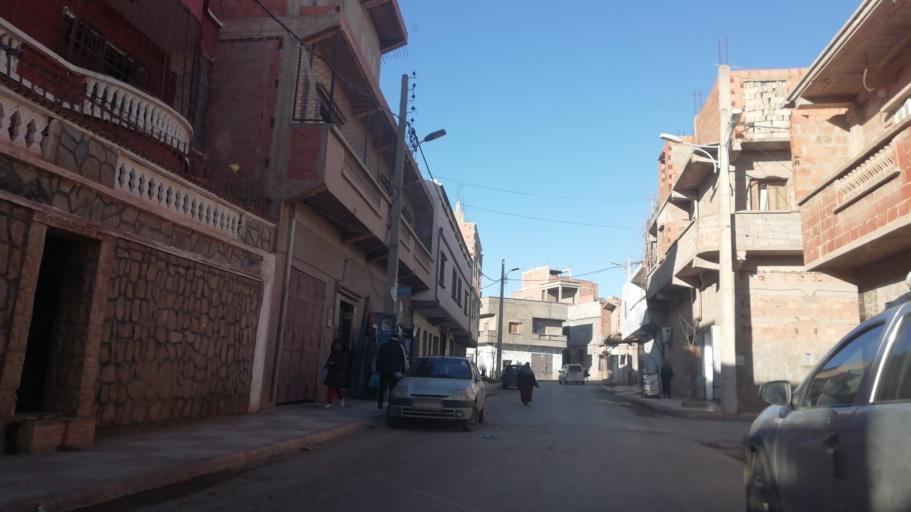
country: DZ
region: Oran
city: Sidi ech Chahmi
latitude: 35.6929
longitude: -0.4943
